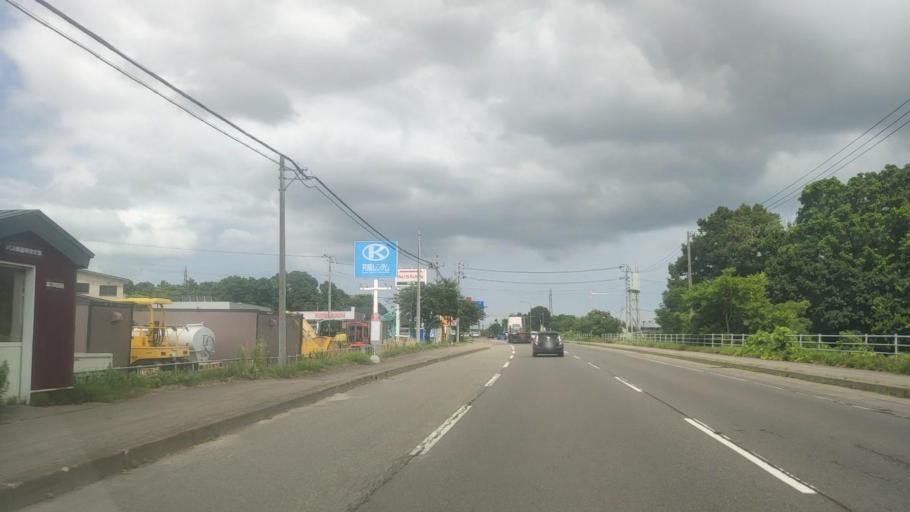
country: JP
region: Hokkaido
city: Nanae
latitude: 42.0890
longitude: 140.5816
